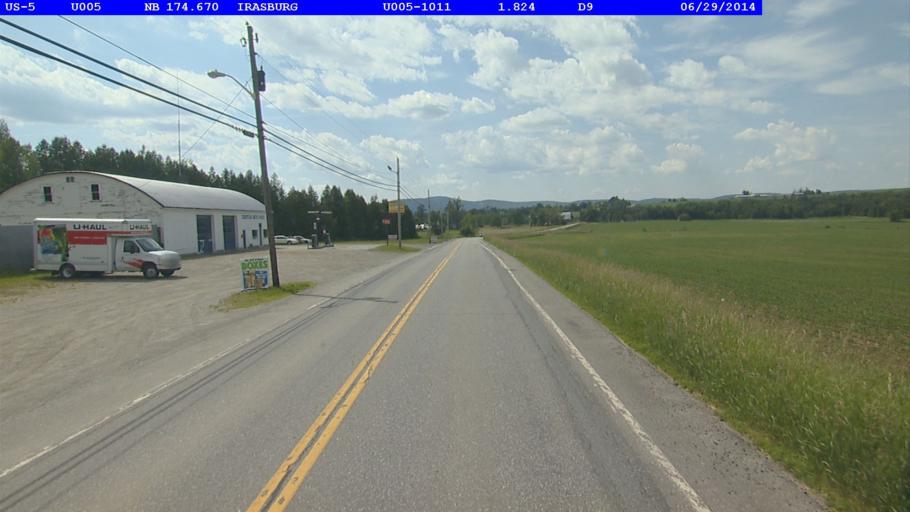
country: US
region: Vermont
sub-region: Orleans County
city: Newport
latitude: 44.8258
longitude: -72.2372
